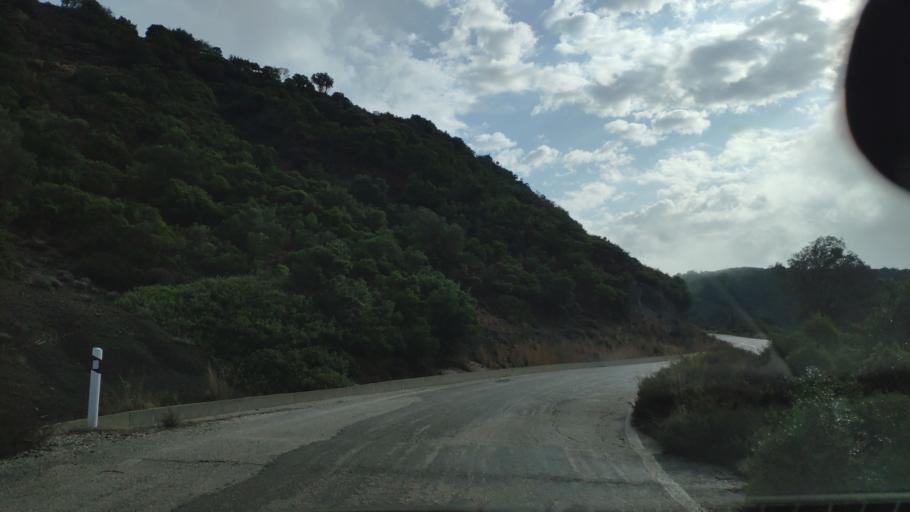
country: GR
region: West Greece
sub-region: Nomos Aitolias kai Akarnanias
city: Sardinia
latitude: 38.8763
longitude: 21.2569
